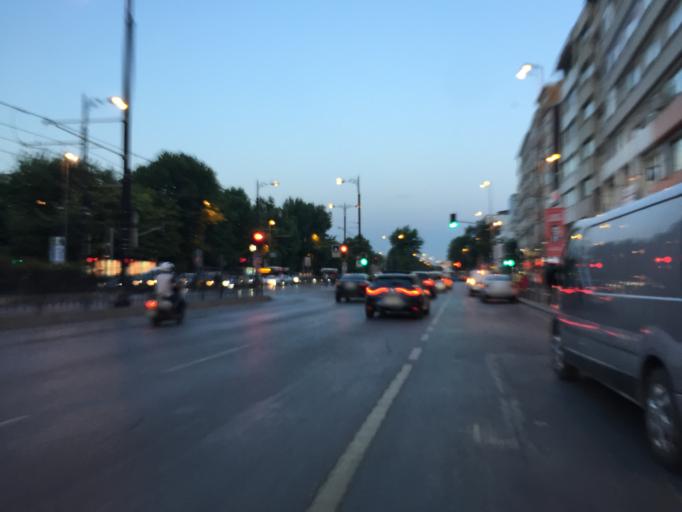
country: TR
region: Istanbul
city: Istanbul
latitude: 41.0165
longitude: 28.9304
